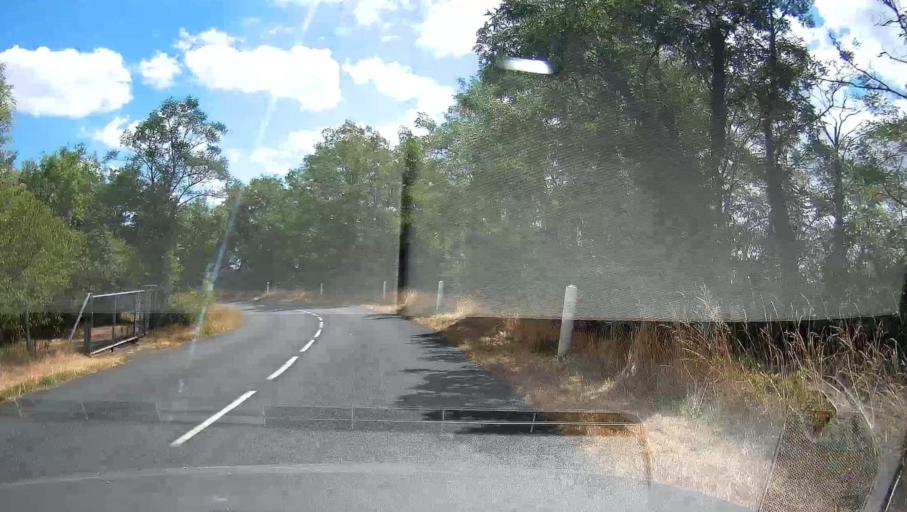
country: FR
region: Rhone-Alpes
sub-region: Departement du Rhone
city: Cogny
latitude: 46.0134
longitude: 4.5801
